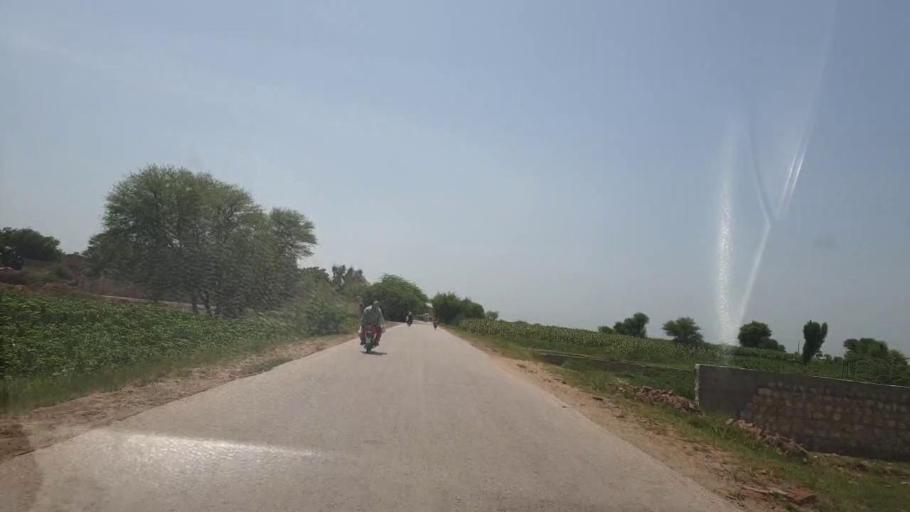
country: PK
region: Sindh
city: Bozdar
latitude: 27.0730
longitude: 68.6010
